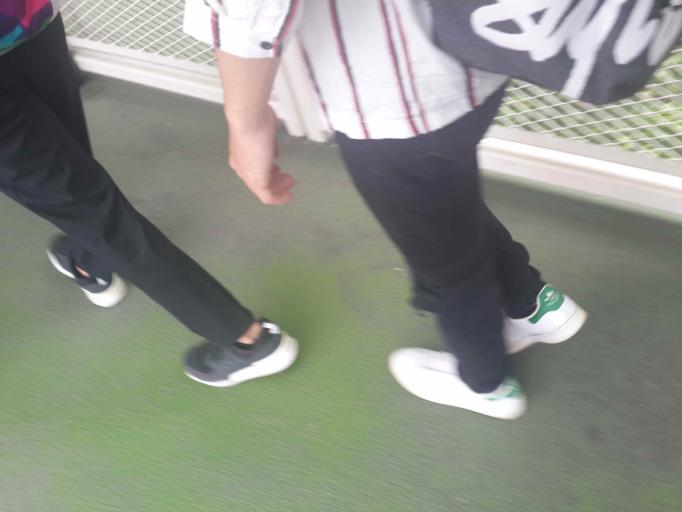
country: MY
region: Selangor
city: Subang Jaya
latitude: 3.0667
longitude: 101.6046
